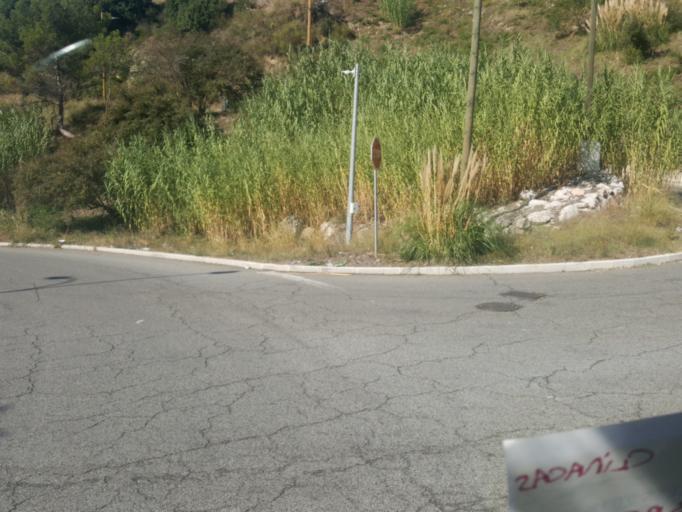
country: FR
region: Provence-Alpes-Cote d'Azur
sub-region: Departement des Alpes-Maritimes
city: Colomars
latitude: 43.7127
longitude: 7.2046
